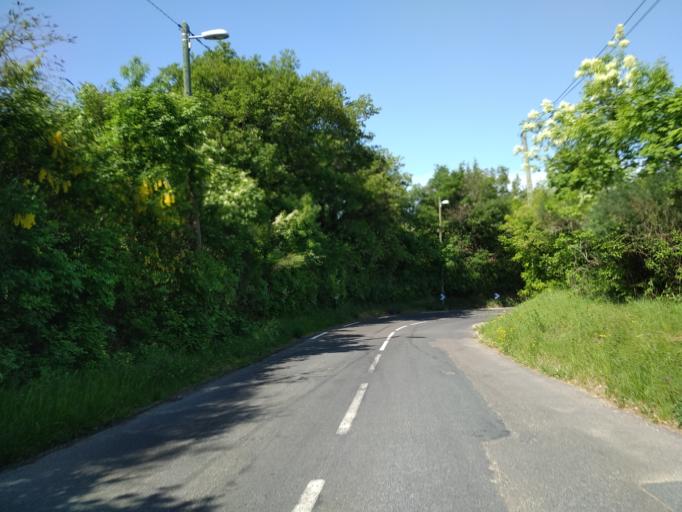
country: FR
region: Rhone-Alpes
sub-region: Departement du Rhone
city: Fontaines-sur-Saone
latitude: 45.8275
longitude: 4.8250
